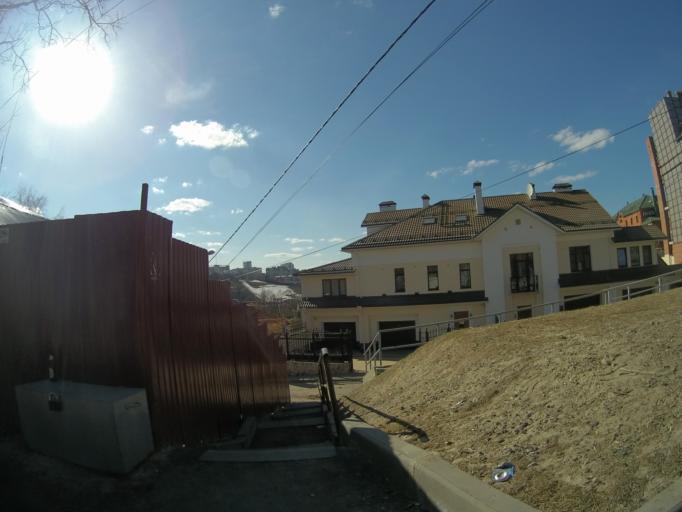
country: RU
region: Vladimir
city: Vladimir
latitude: 56.1236
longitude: 40.3975
